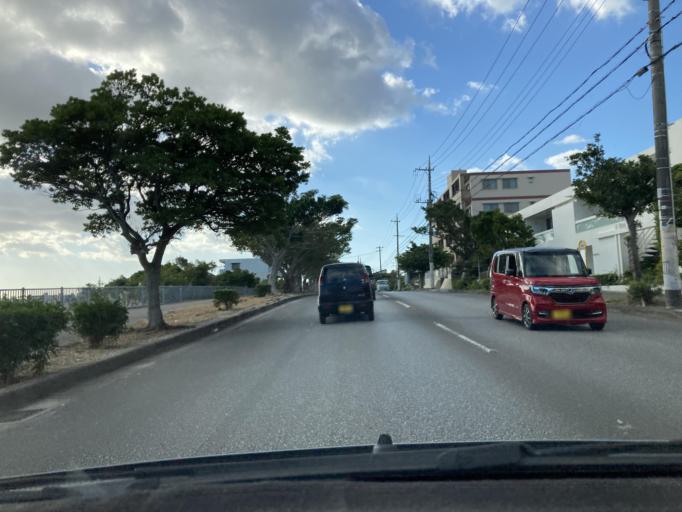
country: JP
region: Okinawa
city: Gushikawa
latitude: 26.3521
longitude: 127.8417
